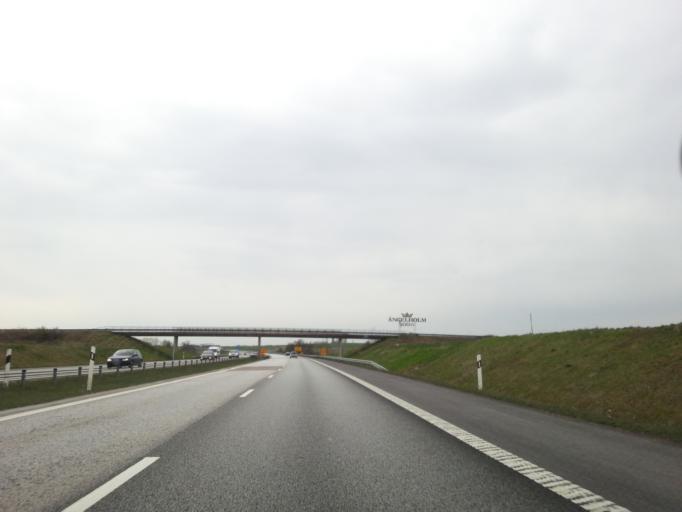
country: SE
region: Skane
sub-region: Angelholms Kommun
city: AEngelholm
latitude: 56.2721
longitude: 12.8944
